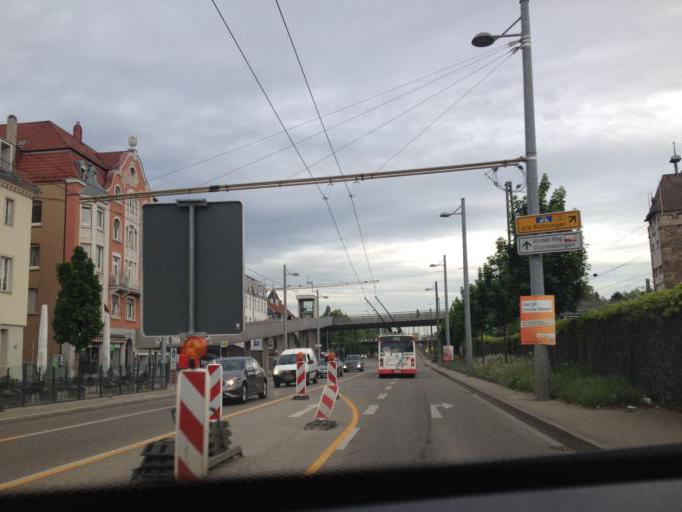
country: DE
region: Baden-Wuerttemberg
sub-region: Regierungsbezirk Stuttgart
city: Esslingen
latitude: 48.7383
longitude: 9.3023
